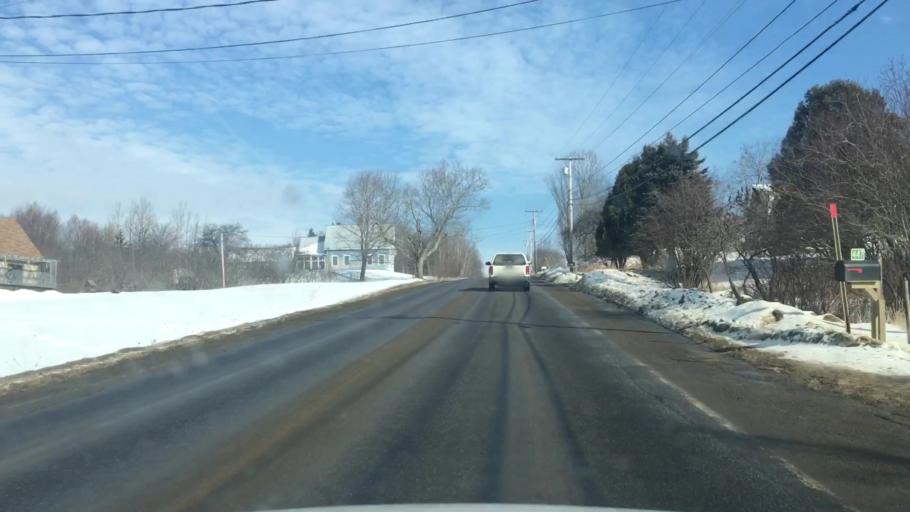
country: US
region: Maine
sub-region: Penobscot County
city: Hermon
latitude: 44.8318
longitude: -68.8810
